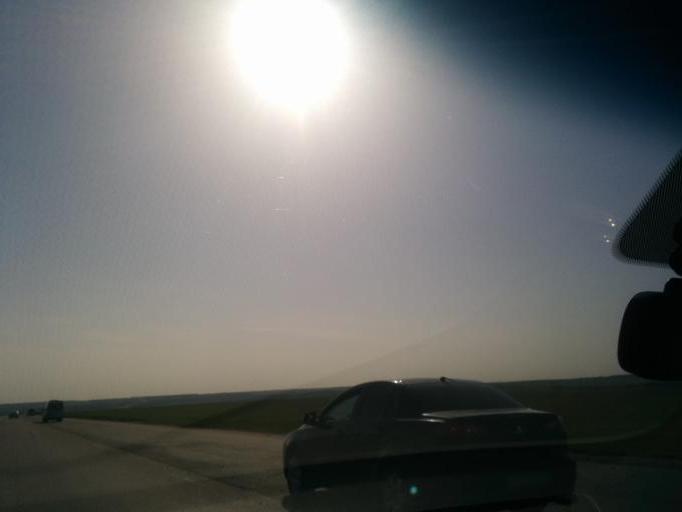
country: RU
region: Rostov
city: Mayskiy
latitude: 47.6729
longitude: 40.0617
